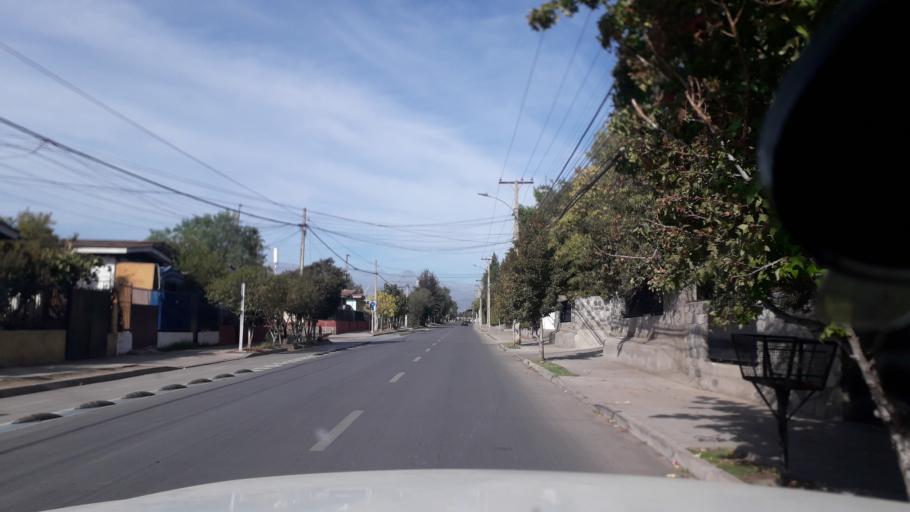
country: CL
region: Valparaiso
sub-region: Provincia de San Felipe
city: San Felipe
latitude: -32.7525
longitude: -70.7153
